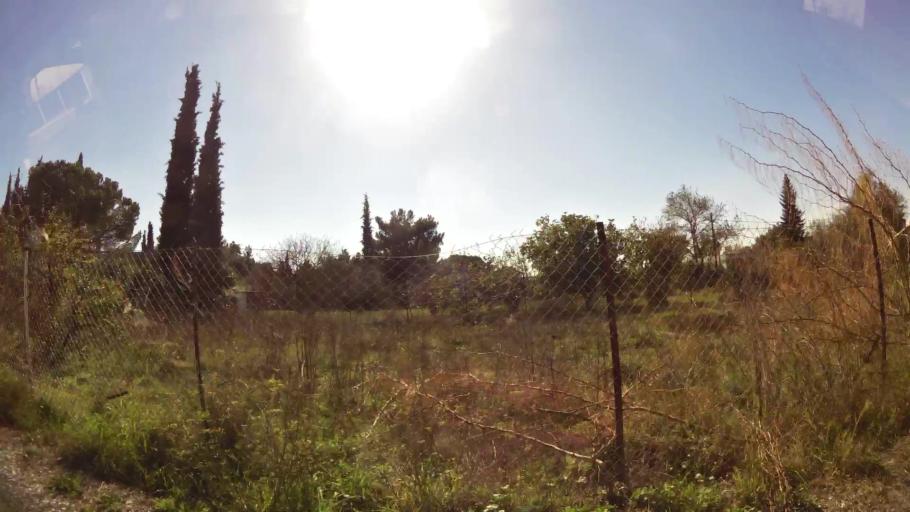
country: GR
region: Attica
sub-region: Nomarchia Athinas
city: Nea Erythraia
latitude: 38.1077
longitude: 23.8237
